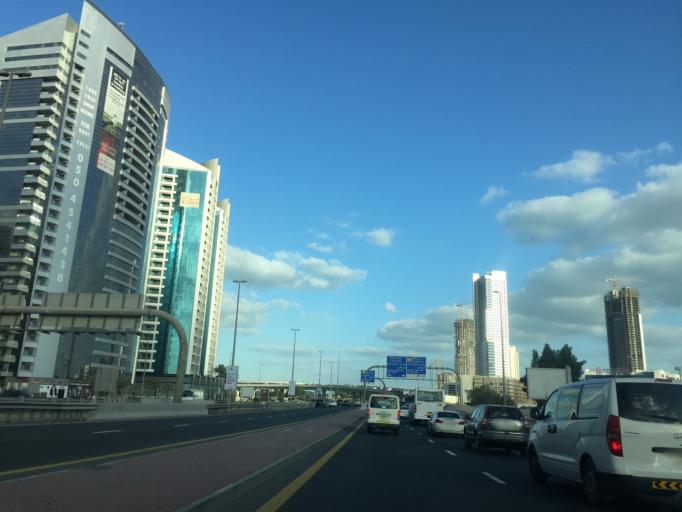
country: AE
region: Dubai
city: Dubai
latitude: 25.1002
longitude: 55.1805
